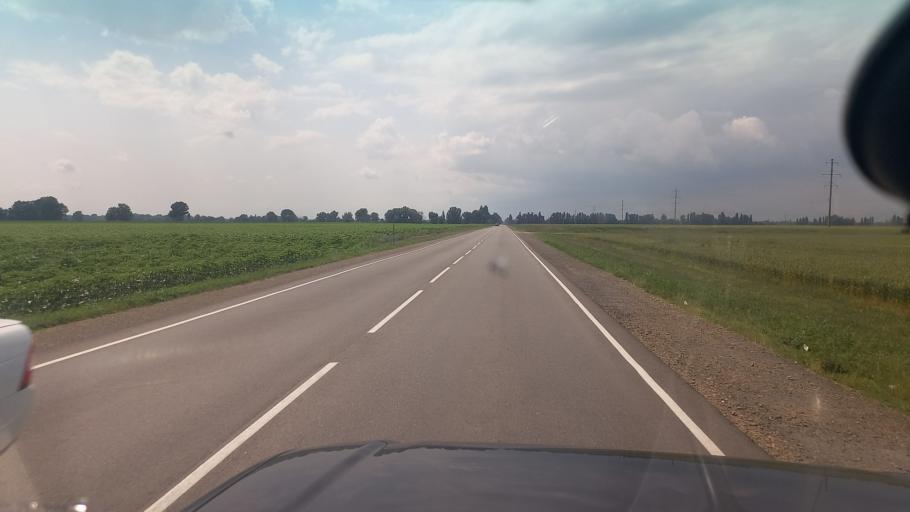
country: RU
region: Adygeya
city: Koshekhabl'
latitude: 44.9075
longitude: 40.4590
